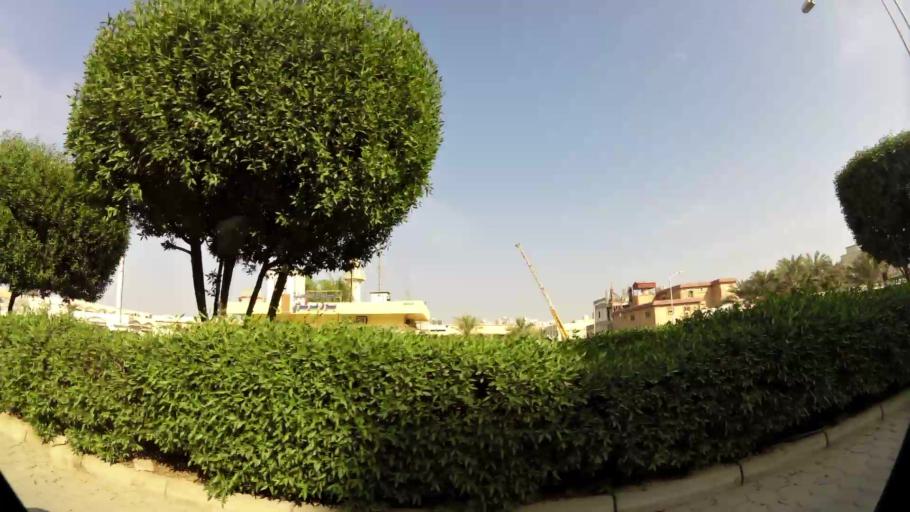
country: KW
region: Al Ahmadi
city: Ar Riqqah
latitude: 29.1545
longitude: 48.1043
